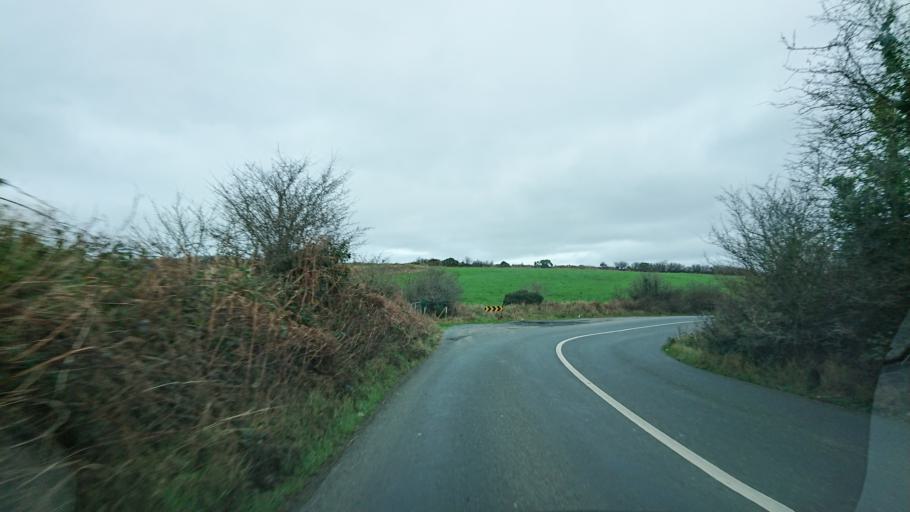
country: IE
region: Leinster
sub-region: Kilkenny
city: Mooncoin
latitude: 52.2132
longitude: -7.2443
